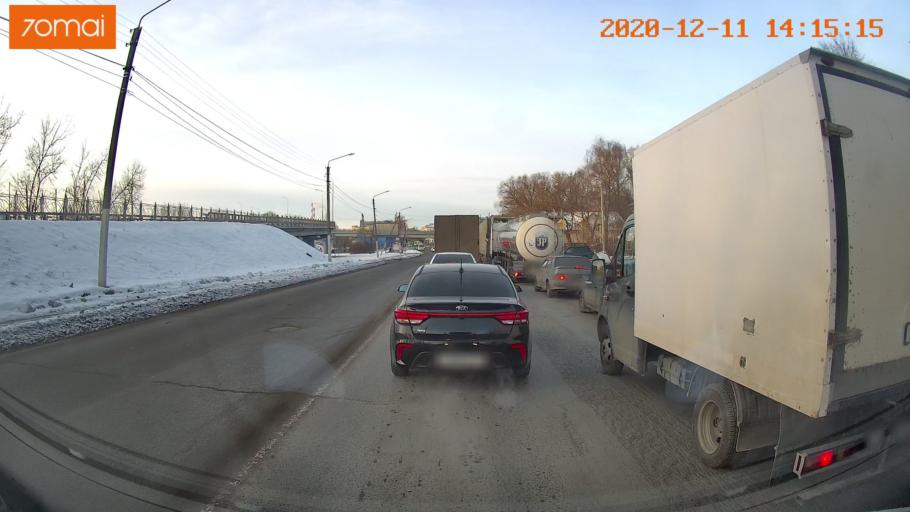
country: RU
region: Kostroma
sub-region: Kostromskoy Rayon
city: Kostroma
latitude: 57.7553
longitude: 40.9479
